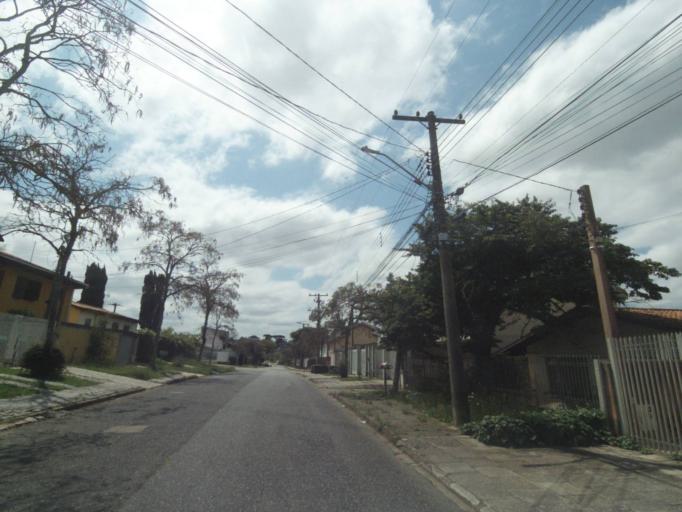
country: BR
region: Parana
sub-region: Pinhais
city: Pinhais
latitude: -25.4158
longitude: -49.2258
